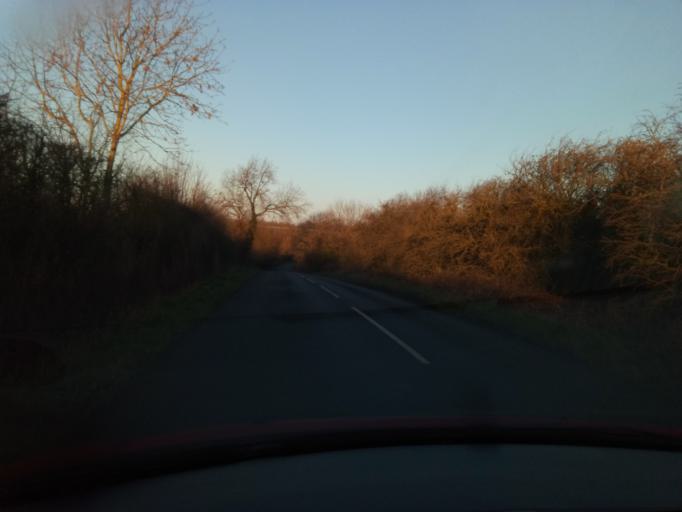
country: GB
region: England
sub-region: Leicestershire
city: Sileby
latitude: 52.7646
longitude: -1.1099
